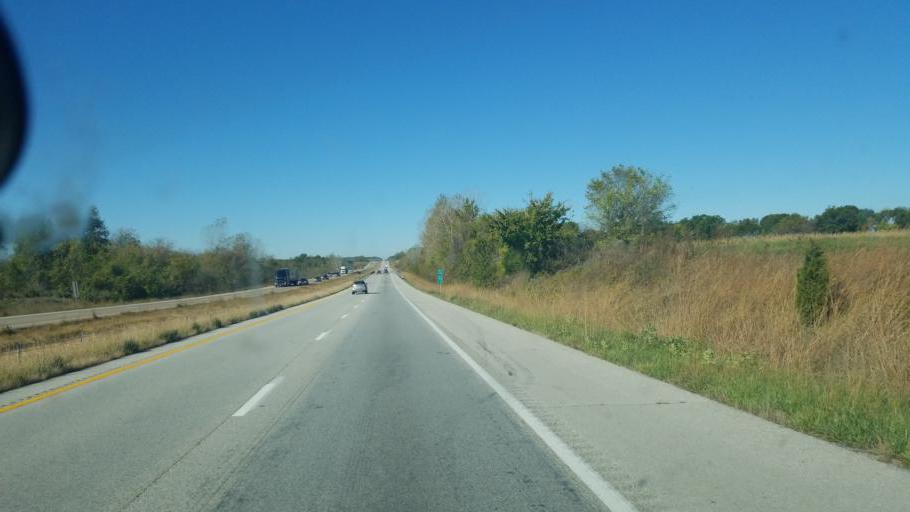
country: US
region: Missouri
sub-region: Cooper County
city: Boonville
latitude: 38.9350
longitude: -92.8959
